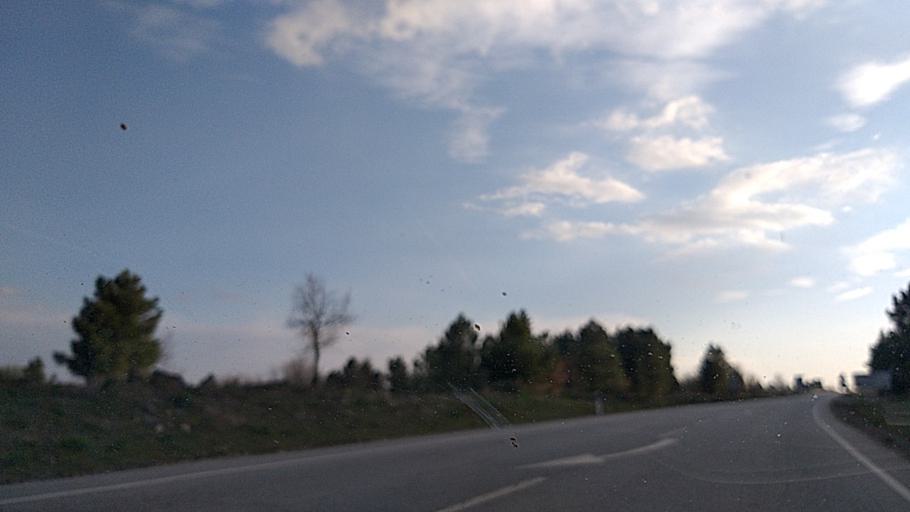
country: ES
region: Castille and Leon
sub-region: Provincia de Salamanca
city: Fuentes de Onoro
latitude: 40.6052
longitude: -6.9840
